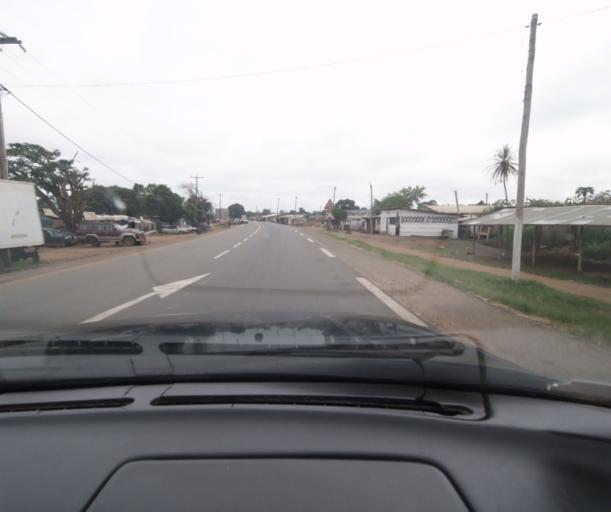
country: CM
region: Centre
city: Saa
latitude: 4.3601
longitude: 11.2752
